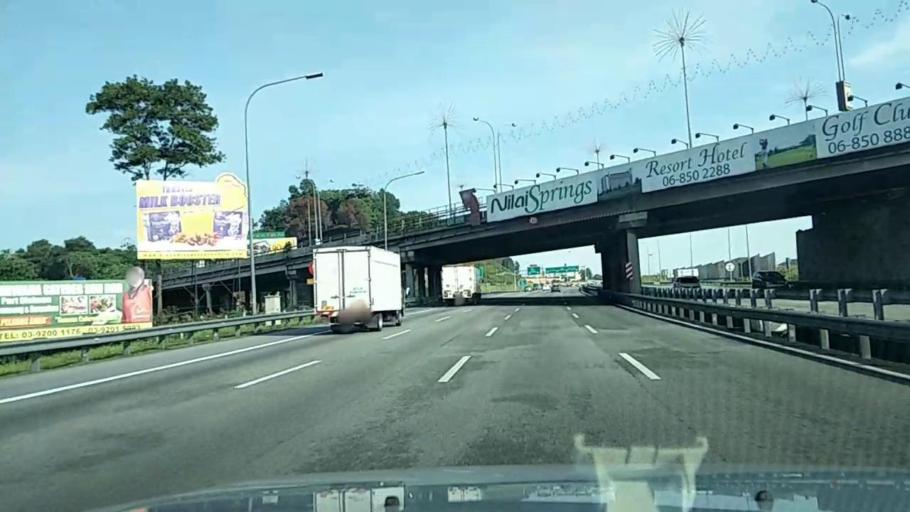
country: MY
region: Negeri Sembilan
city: Kampung Baharu Nilai
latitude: 2.8233
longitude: 101.7980
